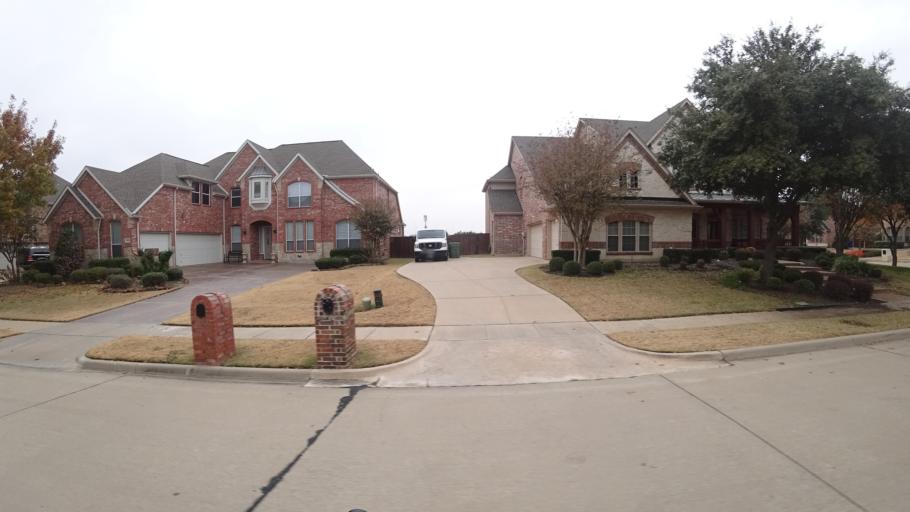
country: US
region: Texas
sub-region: Denton County
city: Lewisville
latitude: 33.0380
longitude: -96.9322
